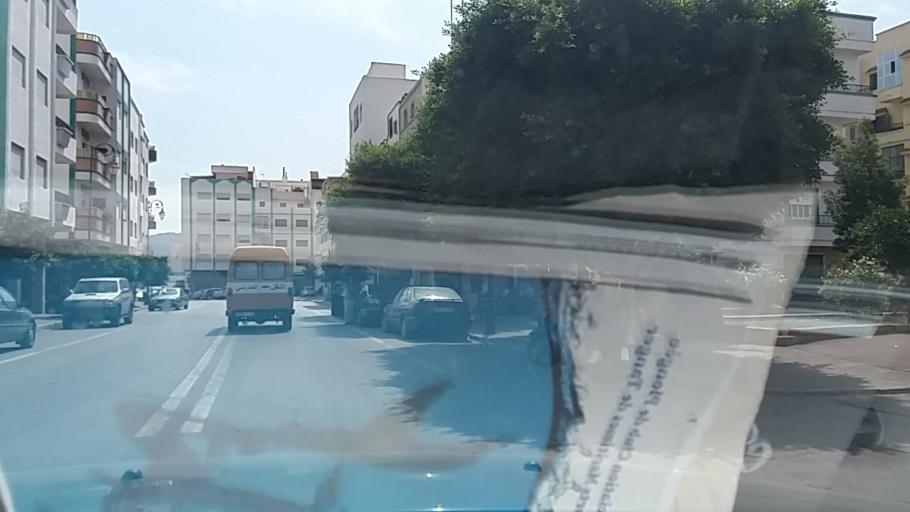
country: MA
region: Tanger-Tetouan
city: Tetouan
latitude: 35.5771
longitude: -5.3439
